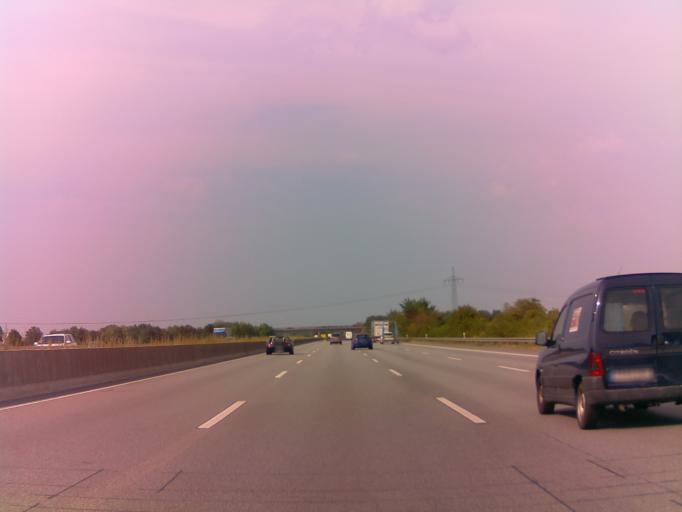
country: DE
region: Hesse
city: Weiterstadt
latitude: 49.9169
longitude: 8.6103
